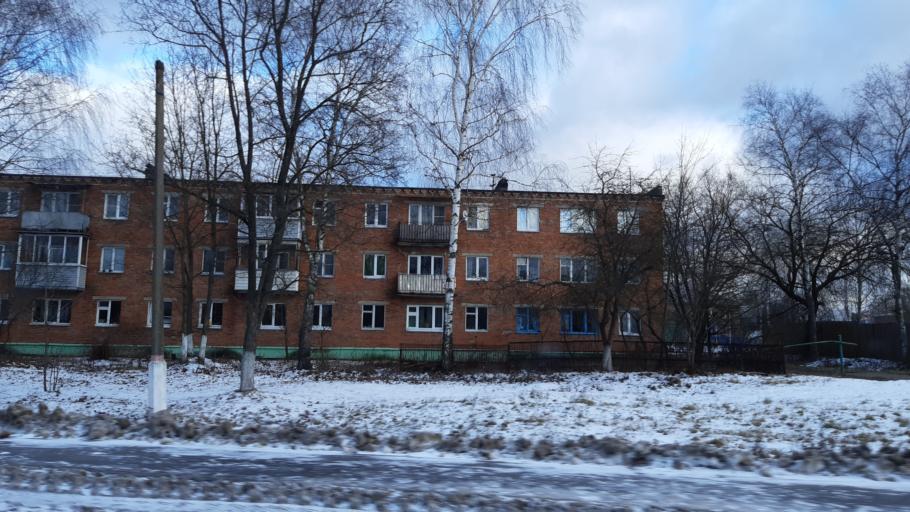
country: RU
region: Moskovskaya
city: Noginsk-9
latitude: 55.9498
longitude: 38.5533
